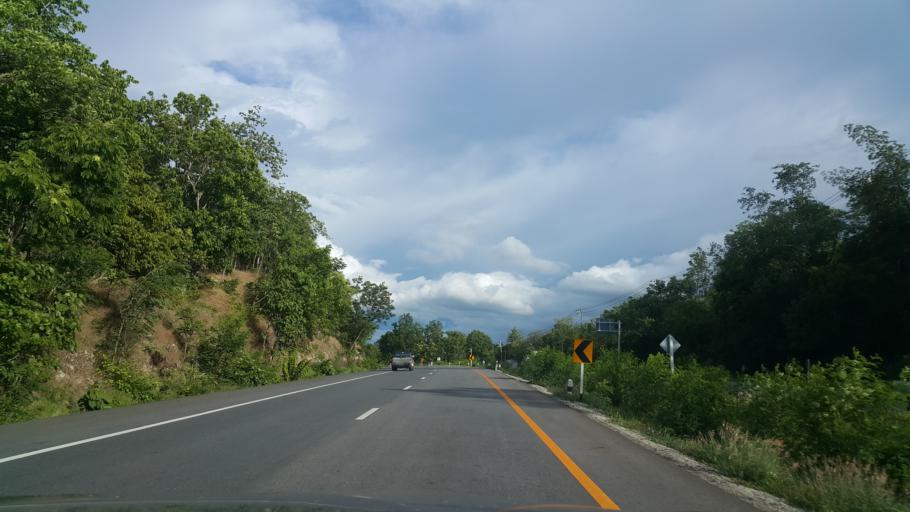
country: TH
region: Tak
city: Ban Tak
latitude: 16.9815
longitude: 99.1218
